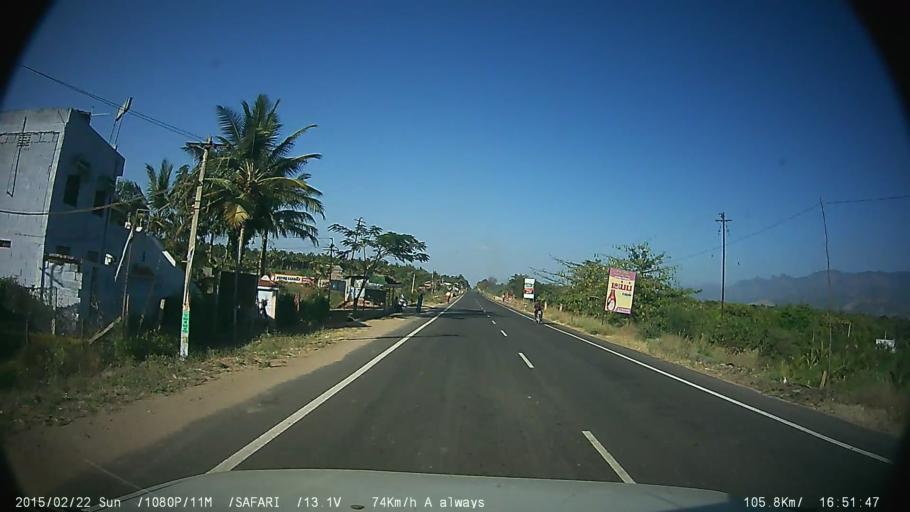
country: IN
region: Tamil Nadu
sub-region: Theni
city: Gudalur
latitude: 9.6522
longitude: 77.2197
